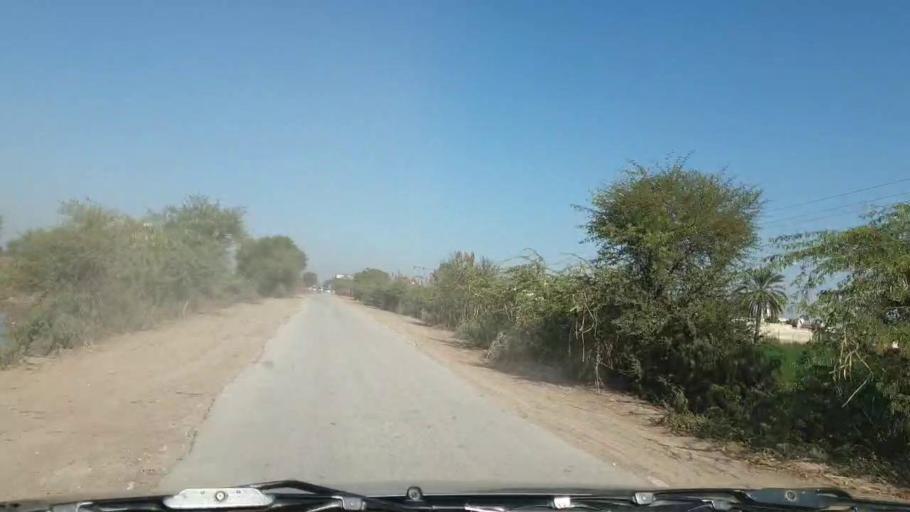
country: PK
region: Sindh
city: Sinjhoro
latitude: 26.1206
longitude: 68.8192
